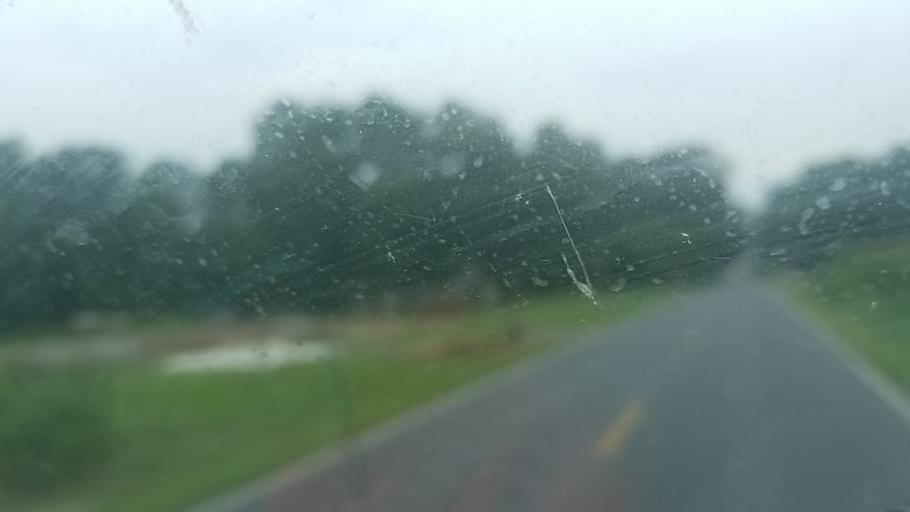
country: US
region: Maryland
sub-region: Wicomico County
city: Salisbury
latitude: 38.3932
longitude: -75.5311
